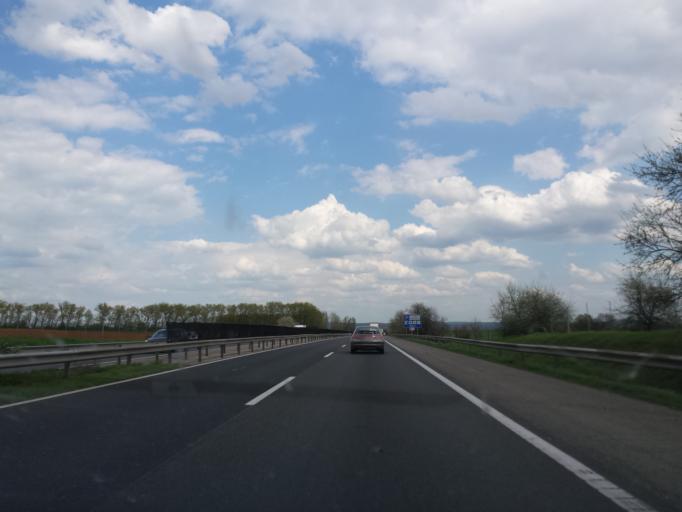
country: HU
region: Pest
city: Zsambek
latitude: 47.5102
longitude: 18.7156
